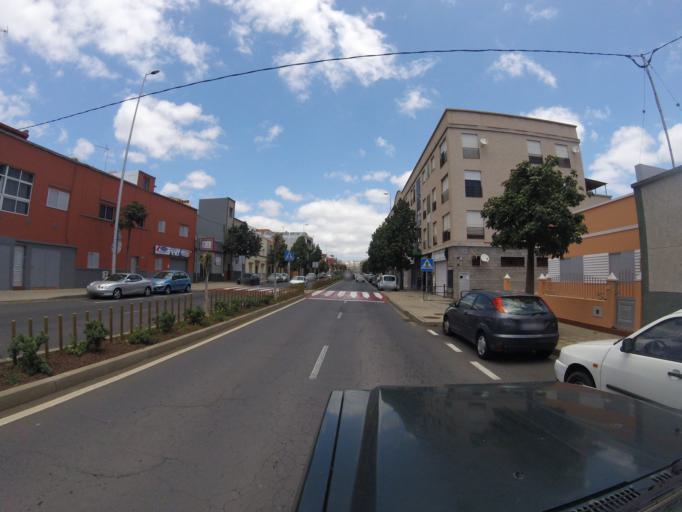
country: ES
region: Canary Islands
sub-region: Provincia de Santa Cruz de Tenerife
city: La Laguna
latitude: 28.4415
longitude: -16.3024
